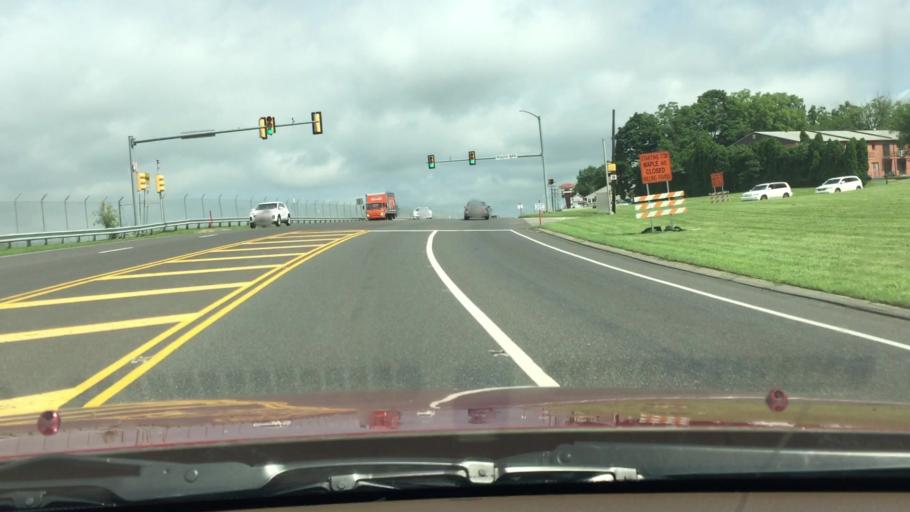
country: US
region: Pennsylvania
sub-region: Montgomery County
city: Horsham
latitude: 40.1906
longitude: -75.1363
